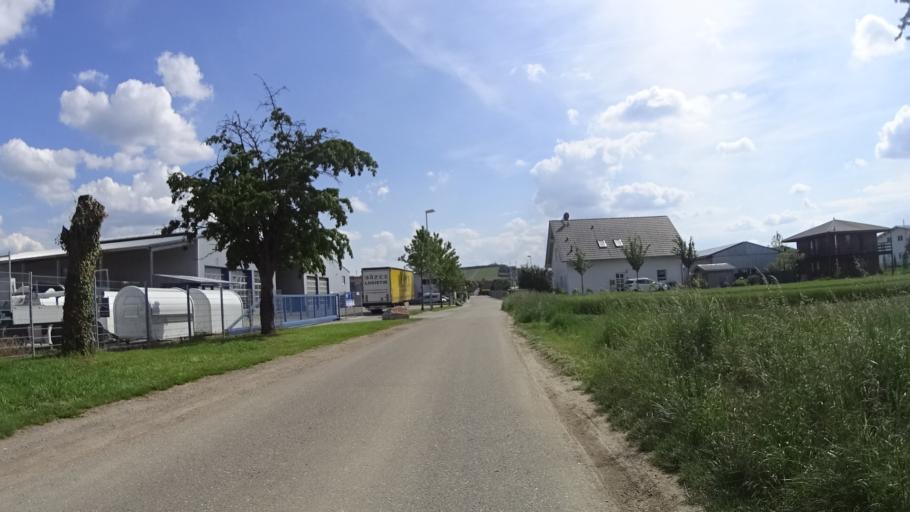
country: DE
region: Baden-Wuerttemberg
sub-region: Freiburg Region
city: Sasbach
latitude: 48.1451
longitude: 7.6198
